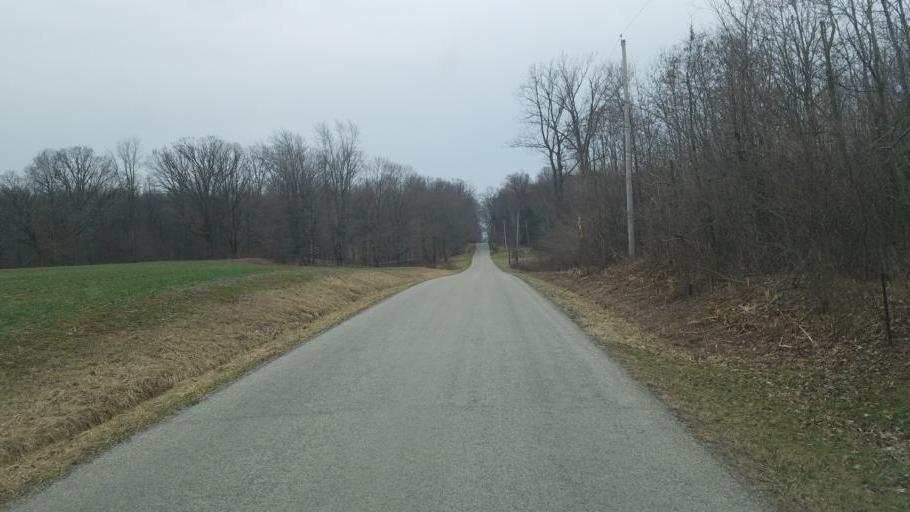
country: US
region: Ohio
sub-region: Crawford County
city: Galion
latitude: 40.6515
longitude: -82.7942
